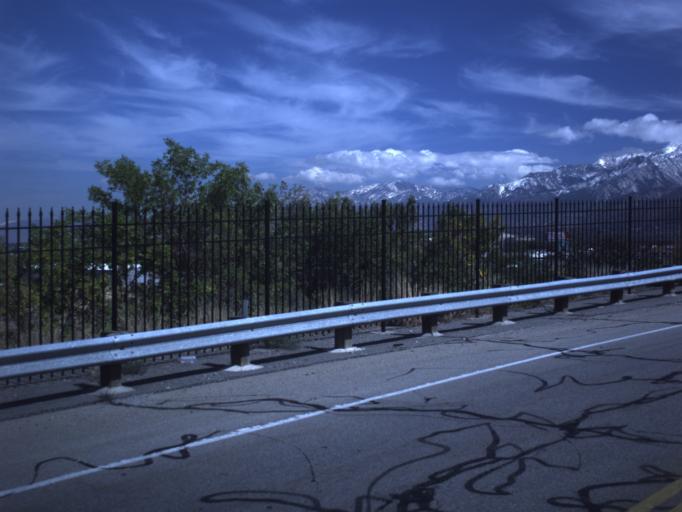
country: US
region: Utah
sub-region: Salt Lake County
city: Bluffdale
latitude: 40.4892
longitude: -111.8949
